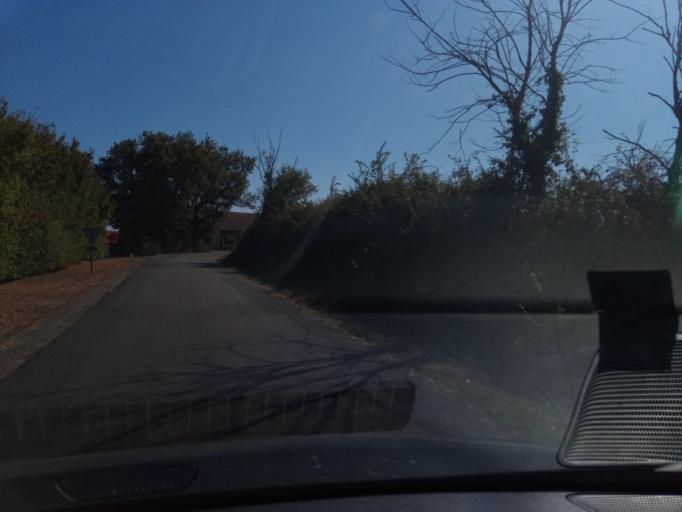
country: FR
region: Poitou-Charentes
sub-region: Departement de la Vienne
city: Lussac-les-Chateaux
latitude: 46.3997
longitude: 0.7424
